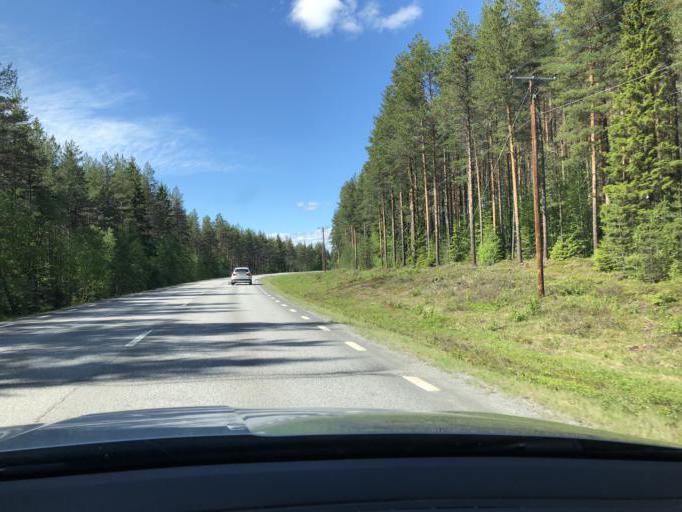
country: SE
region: Norrbotten
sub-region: Alvsbyns Kommun
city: AElvsbyn
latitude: 65.6500
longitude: 21.0903
